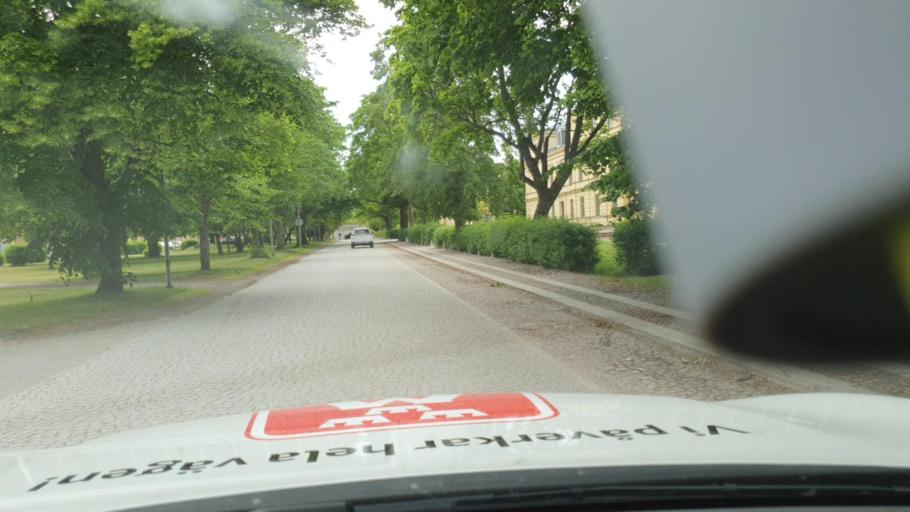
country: SE
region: Vaestra Goetaland
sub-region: Karlsborgs Kommun
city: Karlsborg
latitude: 58.5291
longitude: 14.5269
